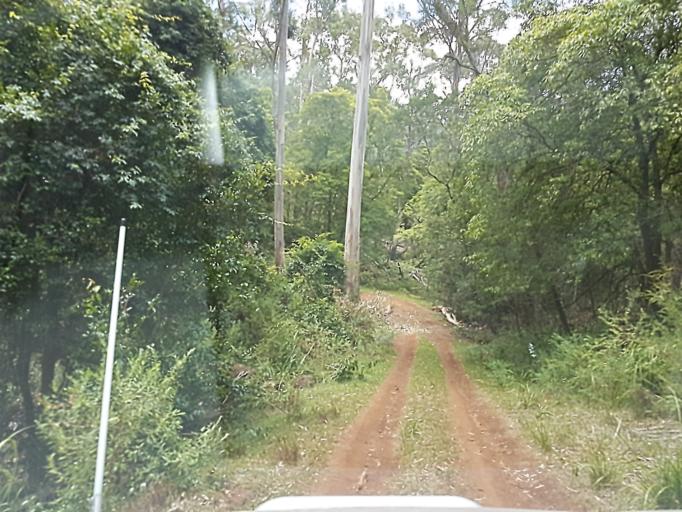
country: AU
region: Victoria
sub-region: East Gippsland
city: Lakes Entrance
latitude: -37.3541
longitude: 148.3571
